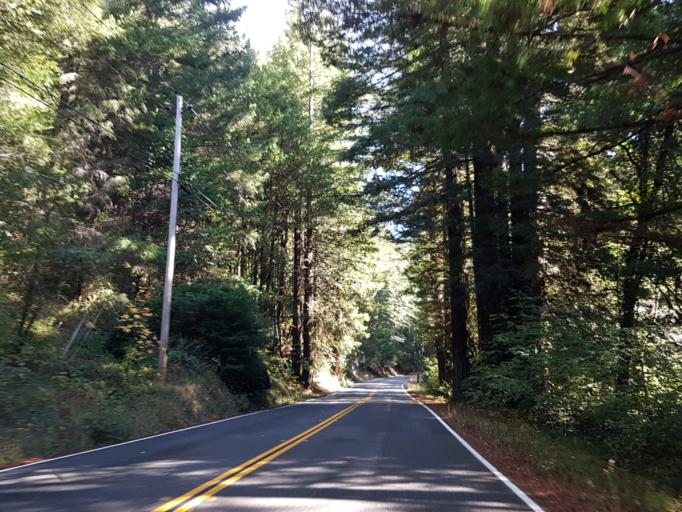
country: US
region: California
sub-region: Humboldt County
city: Rio Dell
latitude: 40.4104
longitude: -123.9565
